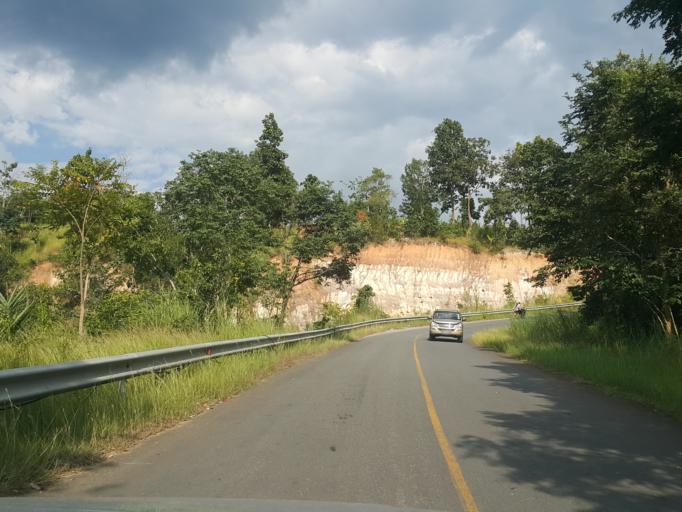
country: TH
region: Chiang Mai
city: Mae Chaem
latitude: 18.5308
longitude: 98.3668
